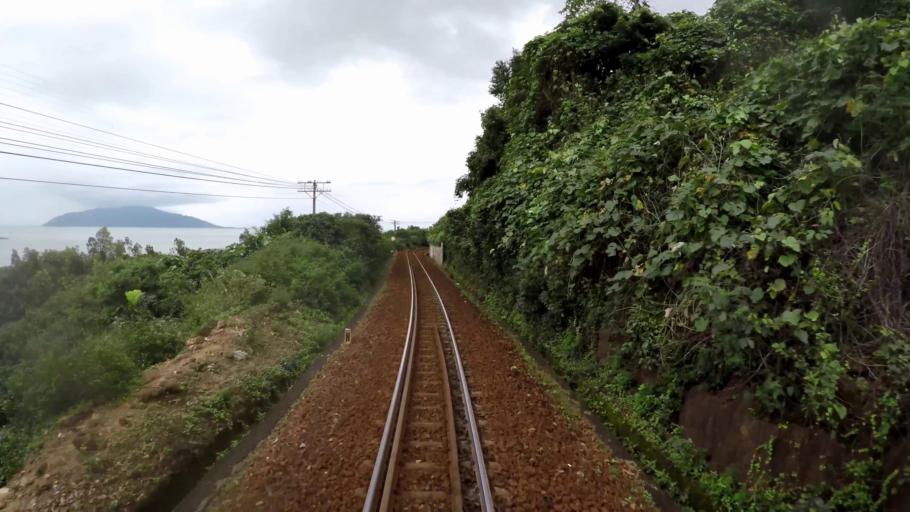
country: VN
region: Da Nang
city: Lien Chieu
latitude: 16.1589
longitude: 108.1348
